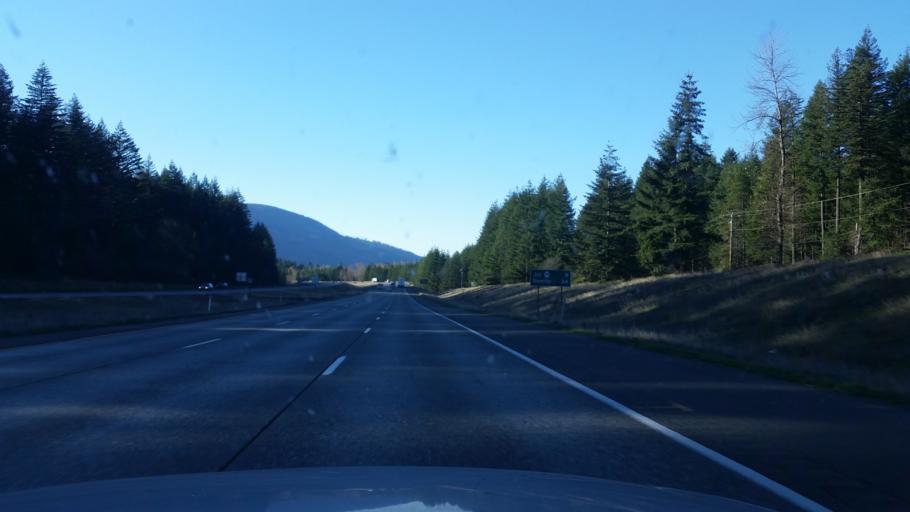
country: US
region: Washington
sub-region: King County
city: Tanner
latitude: 47.4714
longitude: -121.7344
